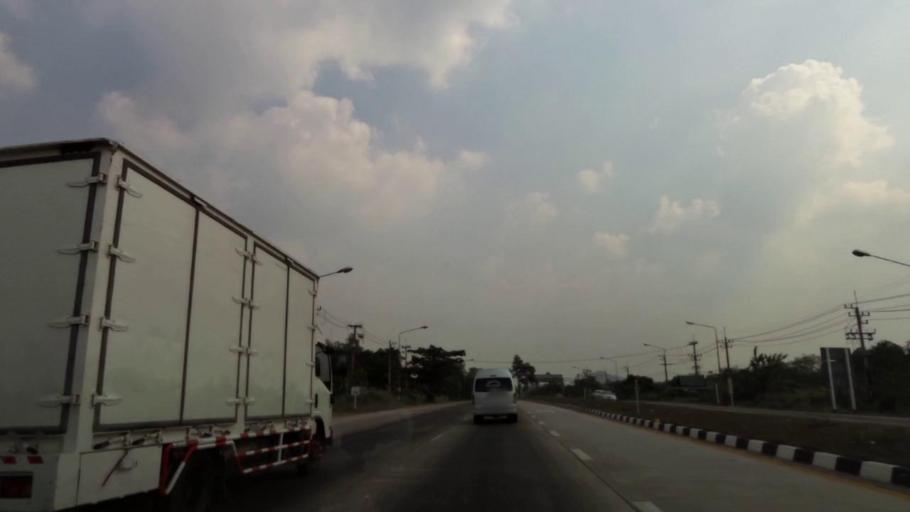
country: TH
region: Chon Buri
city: Nong Yai
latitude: 13.1347
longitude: 101.3493
